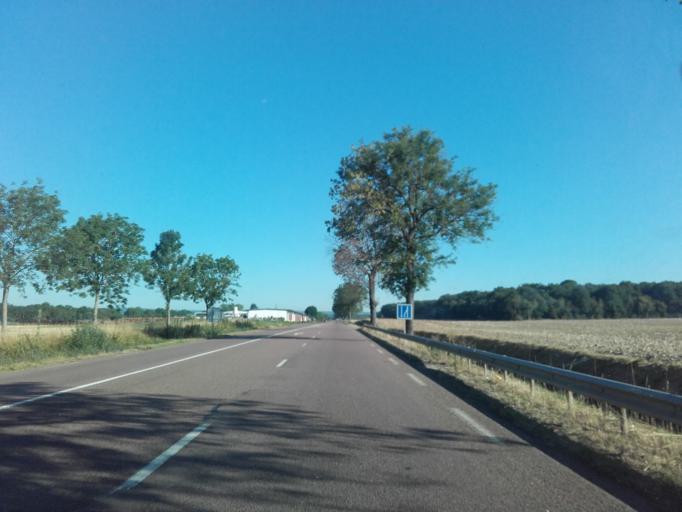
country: FR
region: Bourgogne
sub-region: Departement de Saone-et-Loire
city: Fontaines
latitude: 46.8517
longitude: 4.8059
